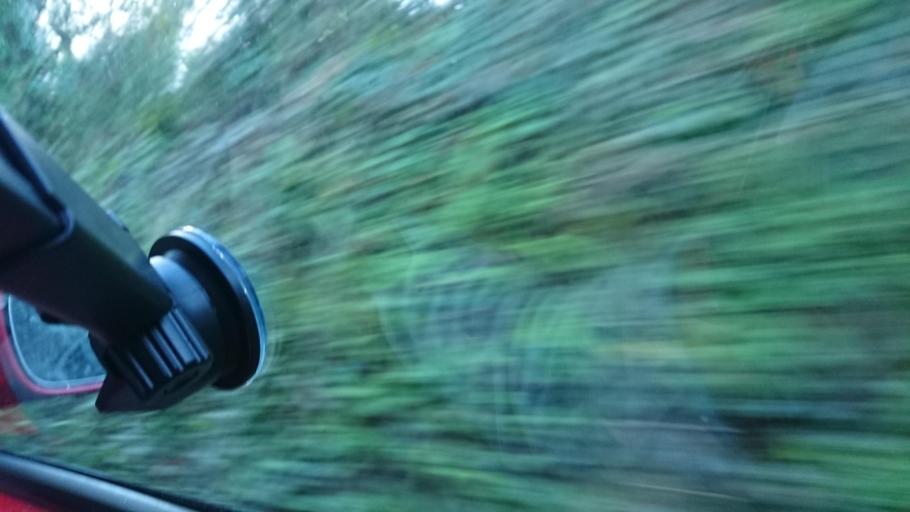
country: GB
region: England
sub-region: Cornwall
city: Looe
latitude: 50.3442
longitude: -4.4780
